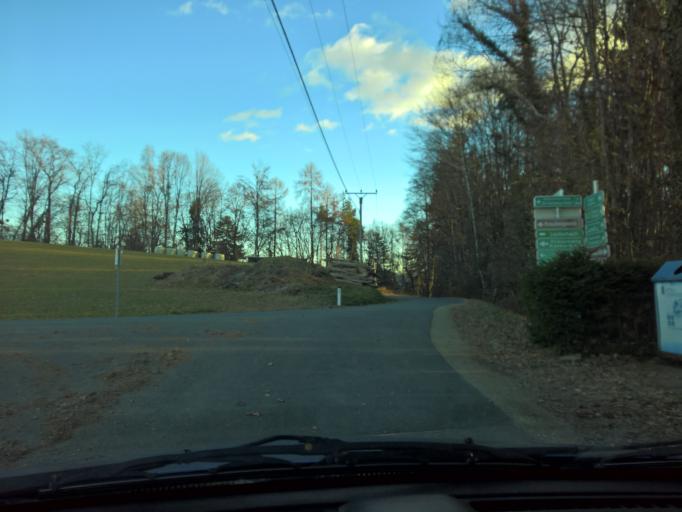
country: AT
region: Styria
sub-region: Politischer Bezirk Leibnitz
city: Sankt Johann im Saggautal
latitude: 46.6974
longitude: 15.4323
